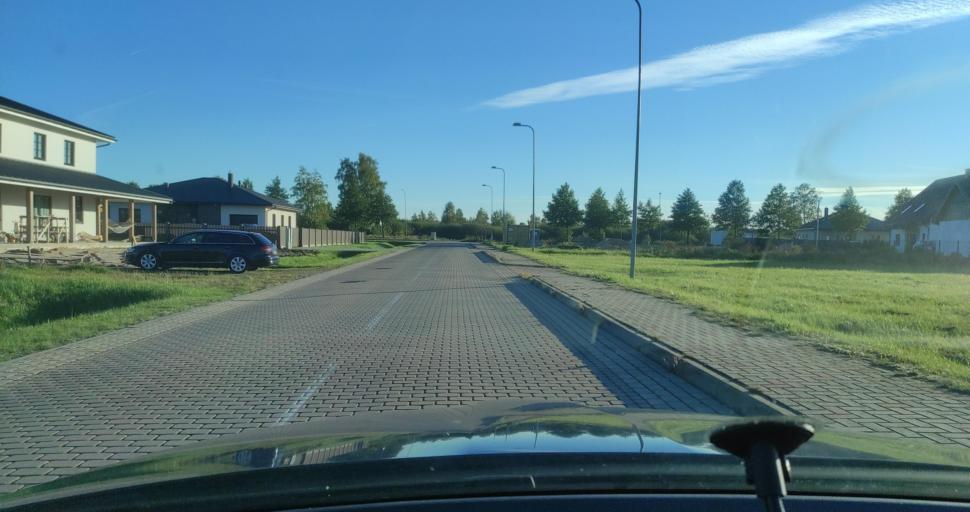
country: LV
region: Ventspils
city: Ventspils
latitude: 57.3664
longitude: 21.5736
